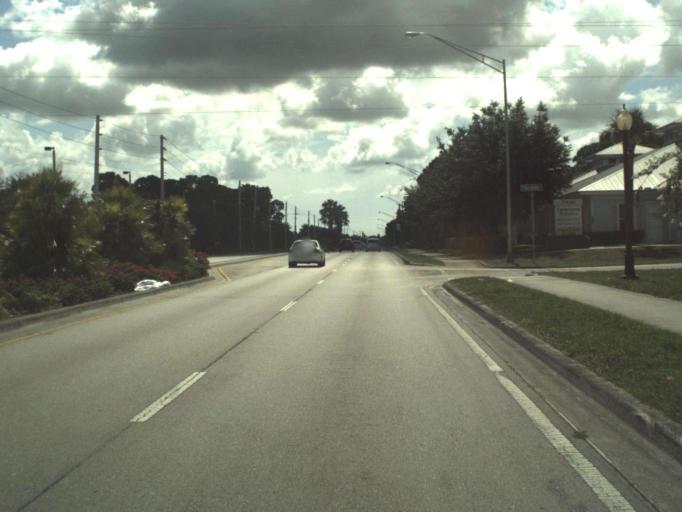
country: US
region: Florida
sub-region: Saint Lucie County
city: River Park
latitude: 27.3177
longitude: -80.3606
